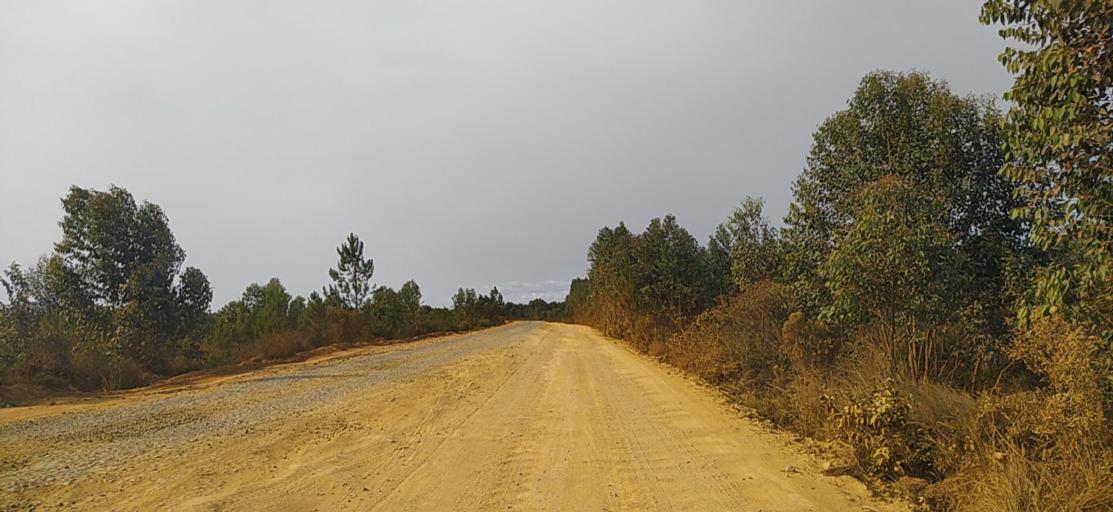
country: MG
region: Alaotra Mangoro
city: Moramanga
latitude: -18.6464
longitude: 48.2751
